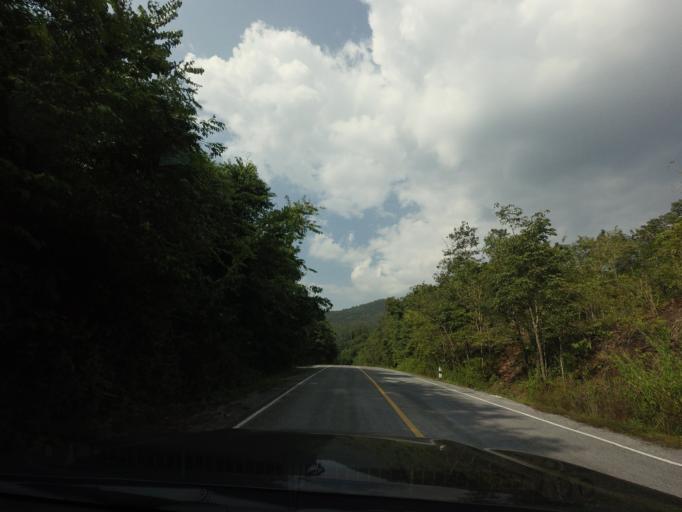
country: TH
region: Uttaradit
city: Ban Khok
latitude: 18.2619
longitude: 100.9927
